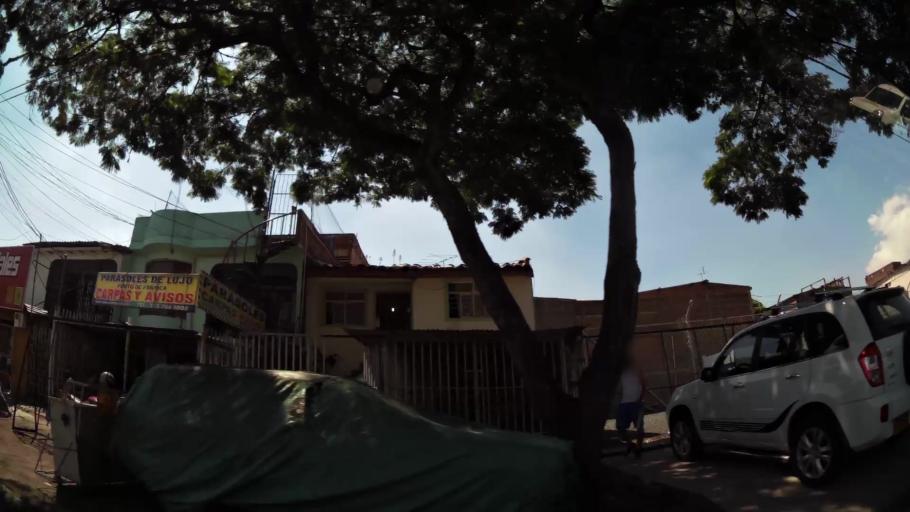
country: CO
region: Valle del Cauca
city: Cali
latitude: 3.4380
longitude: -76.5071
